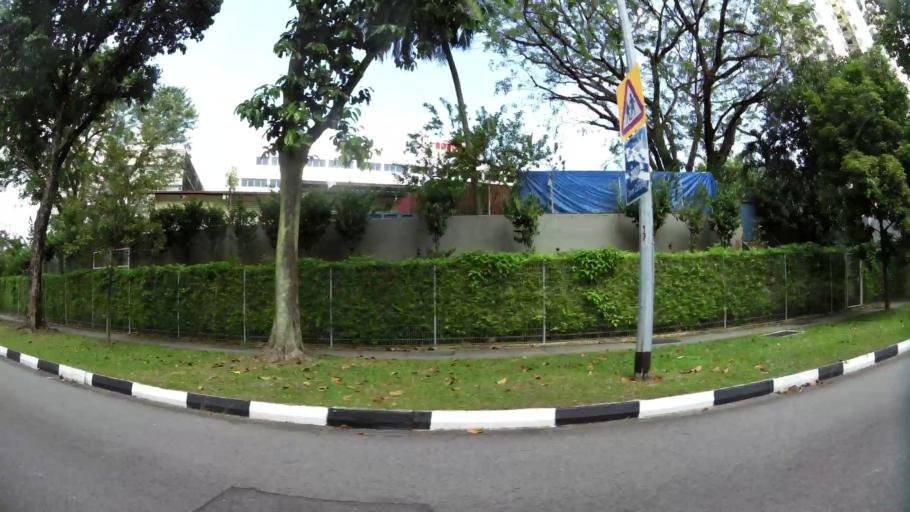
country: SG
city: Singapore
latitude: 1.3470
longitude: 103.8425
